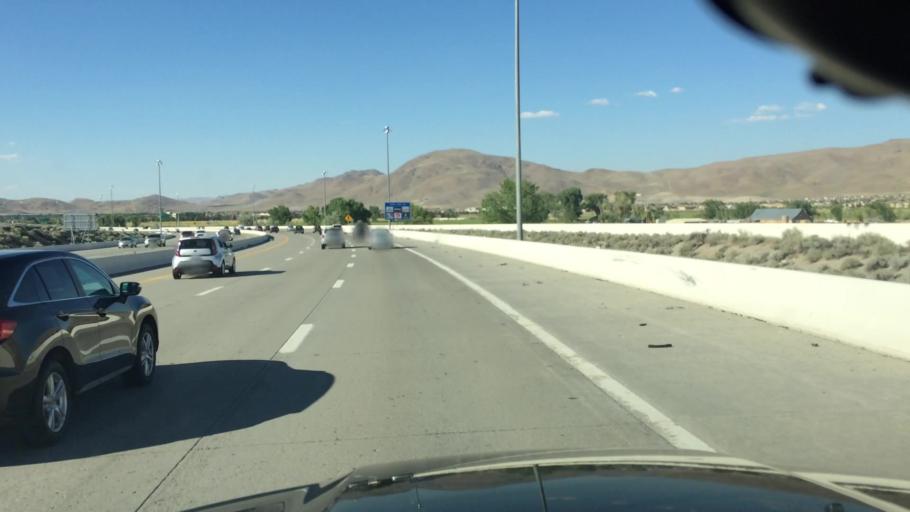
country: US
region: Nevada
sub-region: Washoe County
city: Sparks
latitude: 39.4107
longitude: -119.7483
